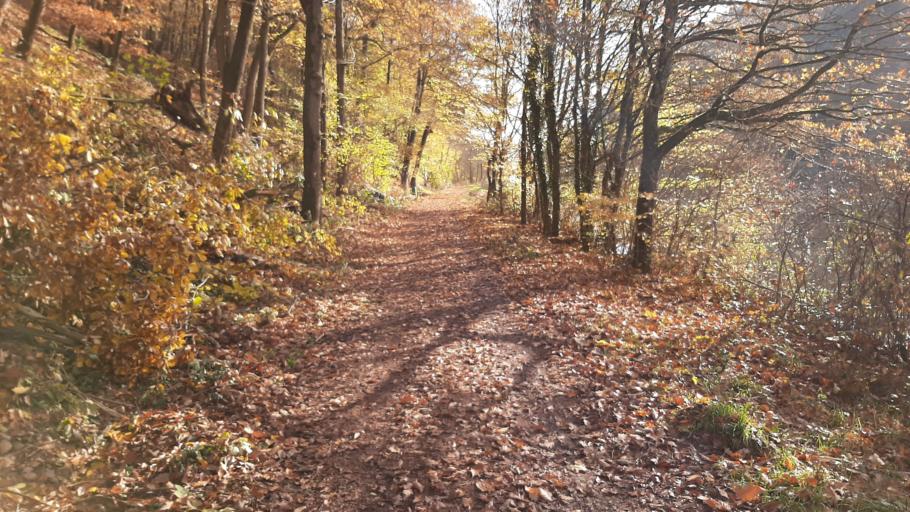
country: DE
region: Saarland
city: Orscholz
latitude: 49.4965
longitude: 6.5504
